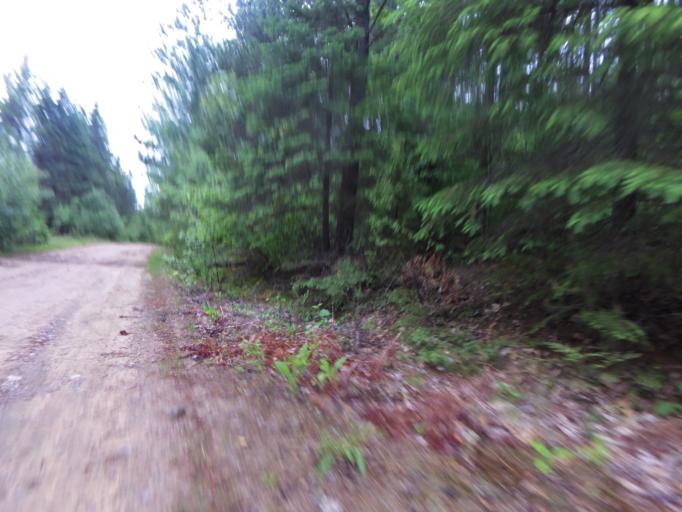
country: CA
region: Quebec
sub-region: Outaouais
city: Shawville
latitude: 45.9092
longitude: -76.2983
